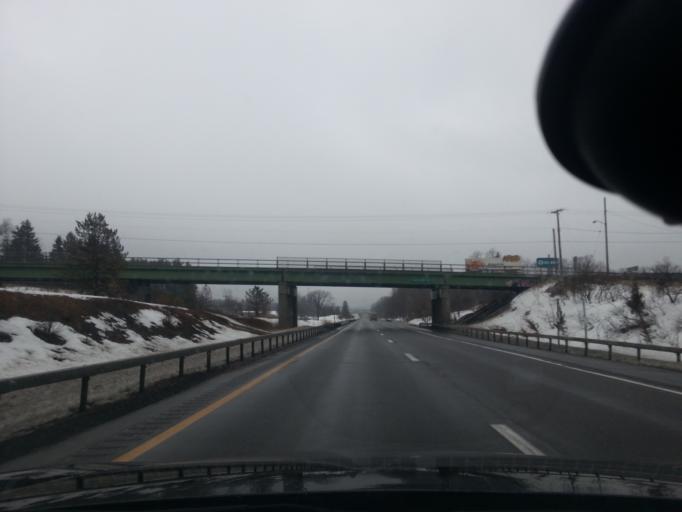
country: US
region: New York
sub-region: Oswego County
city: Pulaski
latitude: 43.5679
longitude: -76.1139
